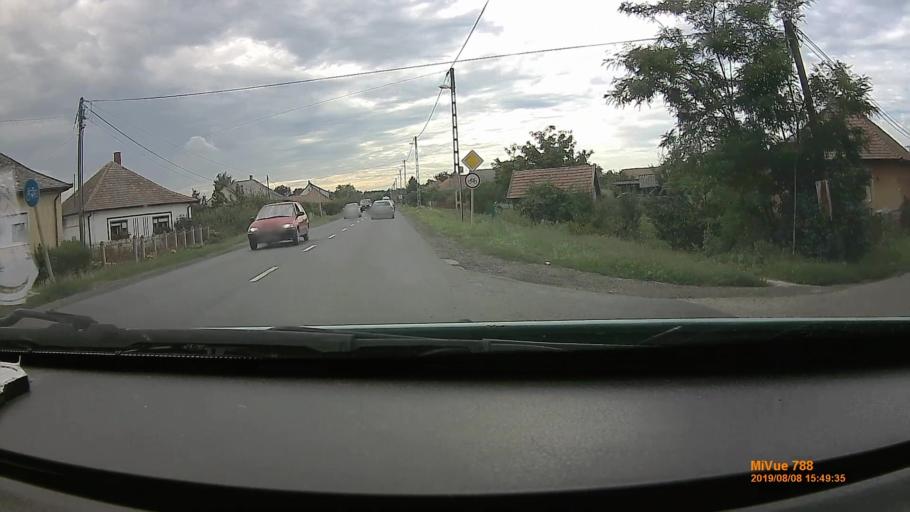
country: HU
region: Szabolcs-Szatmar-Bereg
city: Kocsord
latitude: 47.9432
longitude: 22.3682
